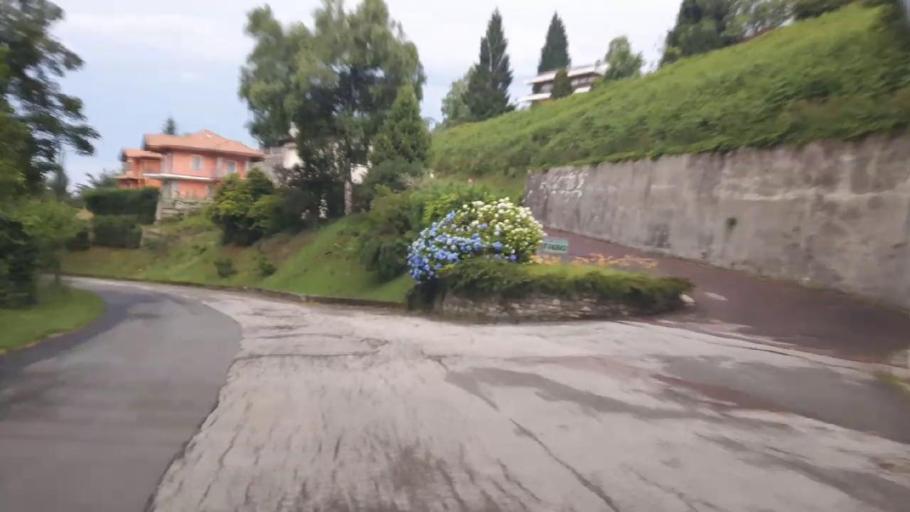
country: IT
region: Piedmont
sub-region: Provincia Verbano-Cusio-Ossola
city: Gignese
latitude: 45.8724
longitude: 8.4973
